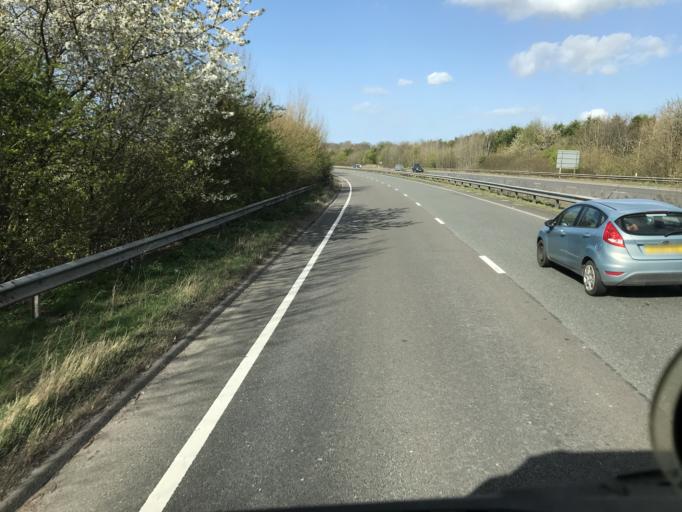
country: GB
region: England
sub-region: Cheshire West and Chester
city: Guilden Sutton
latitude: 53.1873
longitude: -2.8446
